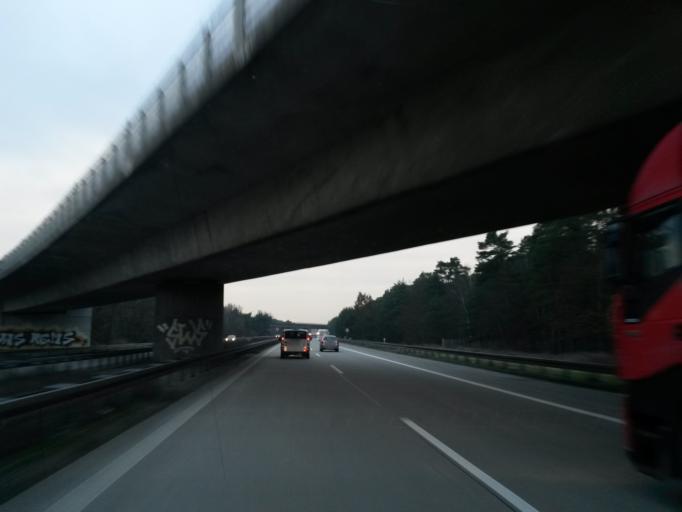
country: DE
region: Baden-Wuerttemberg
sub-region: Karlsruhe Region
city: Hockenheim
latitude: 49.3319
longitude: 8.5603
